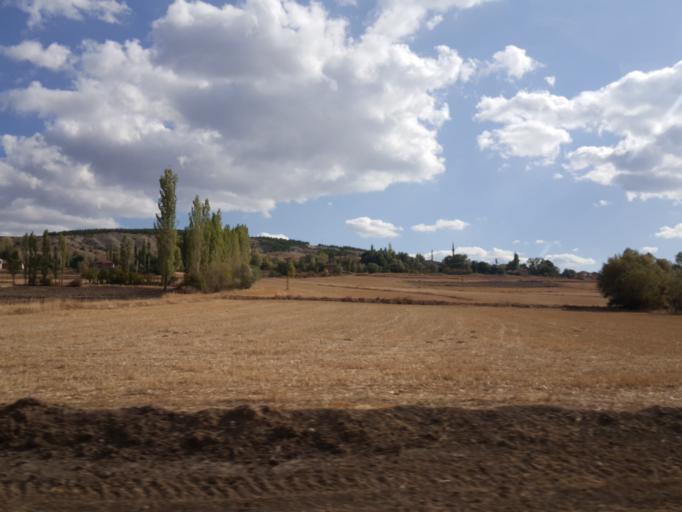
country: TR
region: Tokat
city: Sulusaray
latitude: 39.9885
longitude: 35.9906
